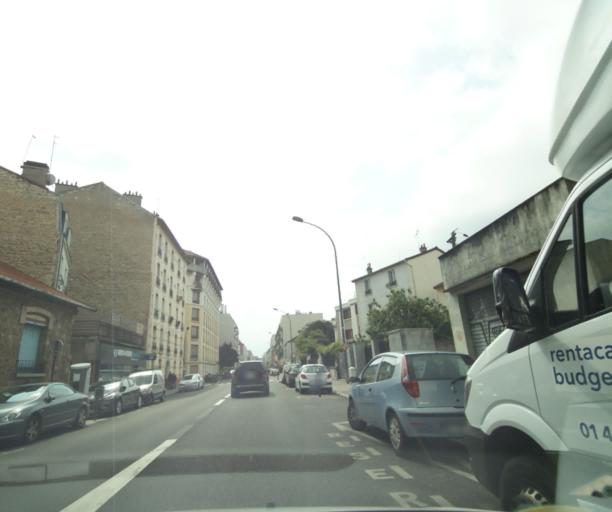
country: FR
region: Ile-de-France
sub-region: Departement des Hauts-de-Seine
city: Asnieres-sur-Seine
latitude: 48.9177
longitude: 2.2816
